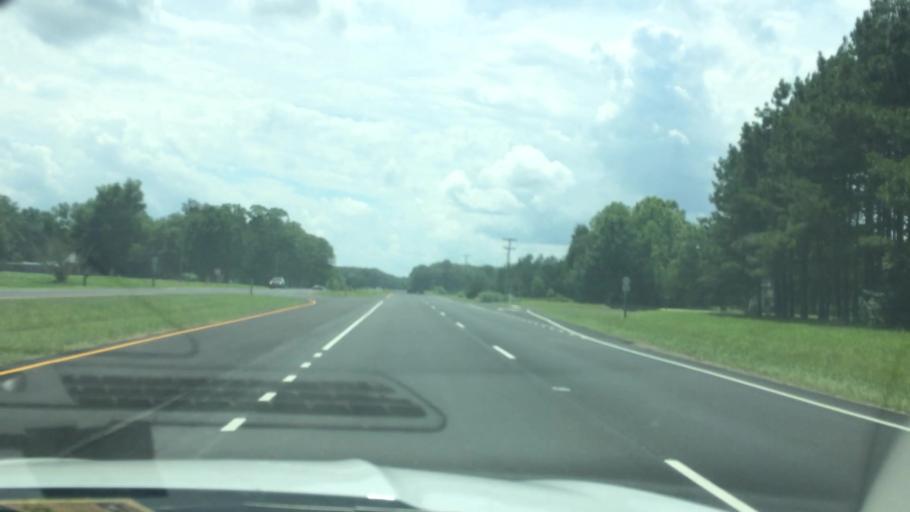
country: US
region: Virginia
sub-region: Middlesex County
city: Saluda
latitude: 37.5508
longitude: -76.6806
